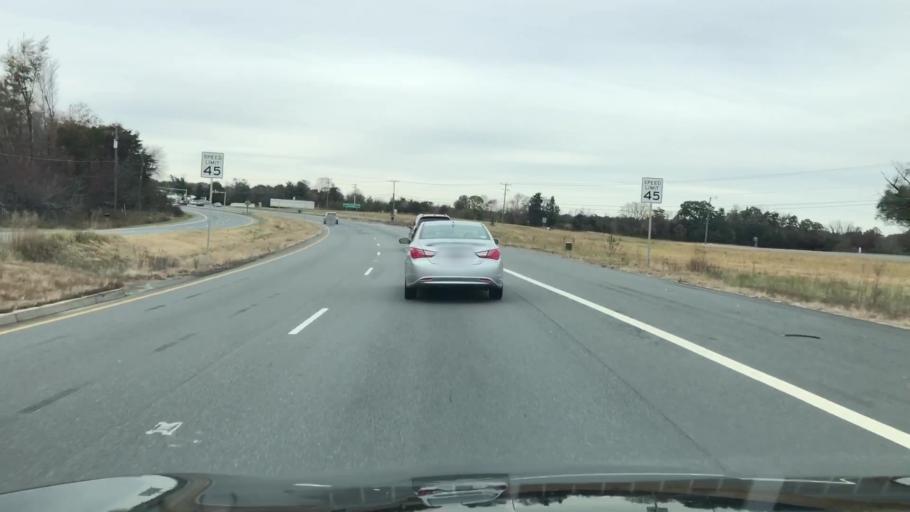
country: US
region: Virginia
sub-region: Stafford County
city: Falmouth
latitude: 38.3670
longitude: -77.5221
